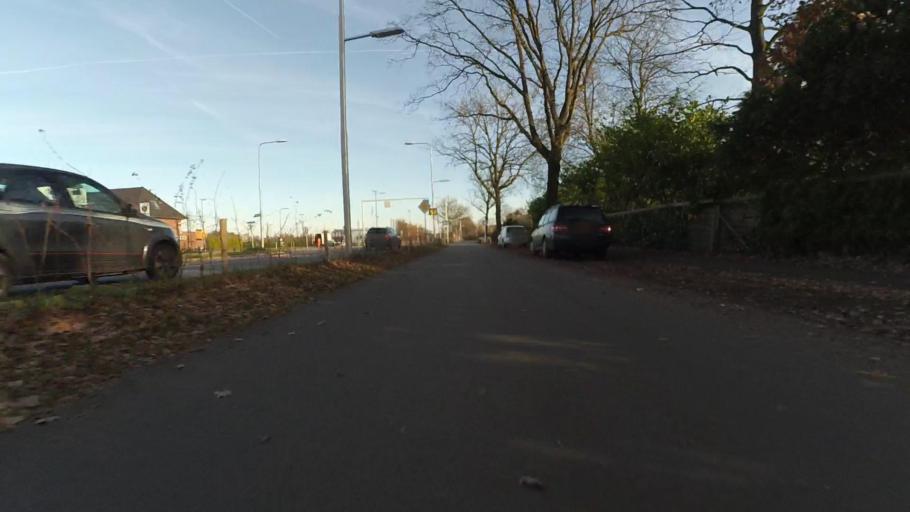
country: NL
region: Utrecht
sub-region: Gemeente Utrechtse Heuvelrug
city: Doorn
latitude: 52.0147
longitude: 5.3305
